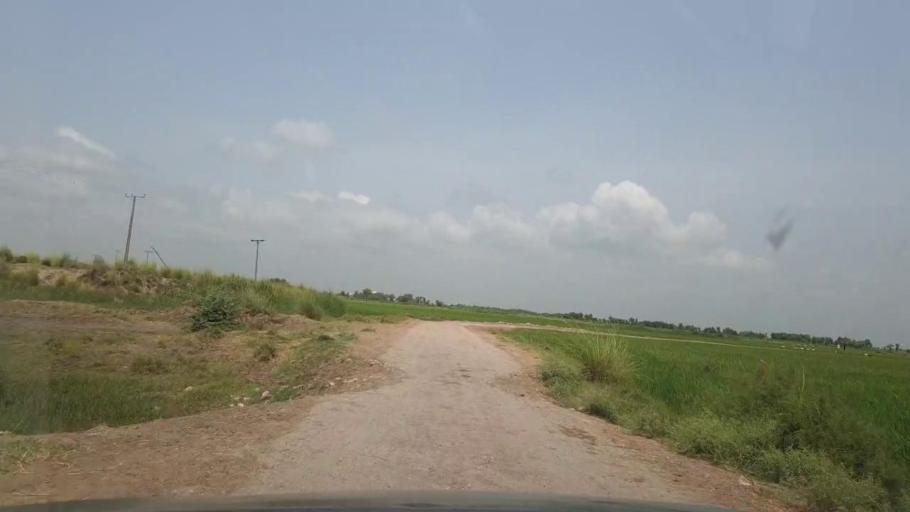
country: PK
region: Sindh
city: Ratodero
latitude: 27.9143
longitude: 68.2988
